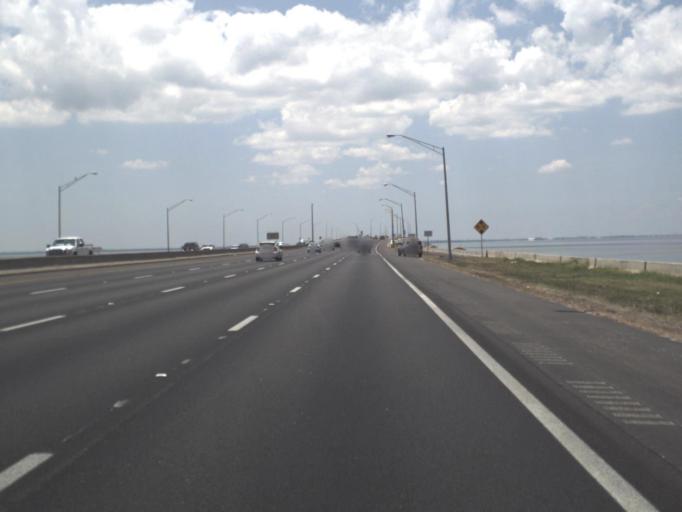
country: US
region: Florida
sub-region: Hillsborough County
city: Town 'n' Country
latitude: 27.9382
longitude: -82.5584
